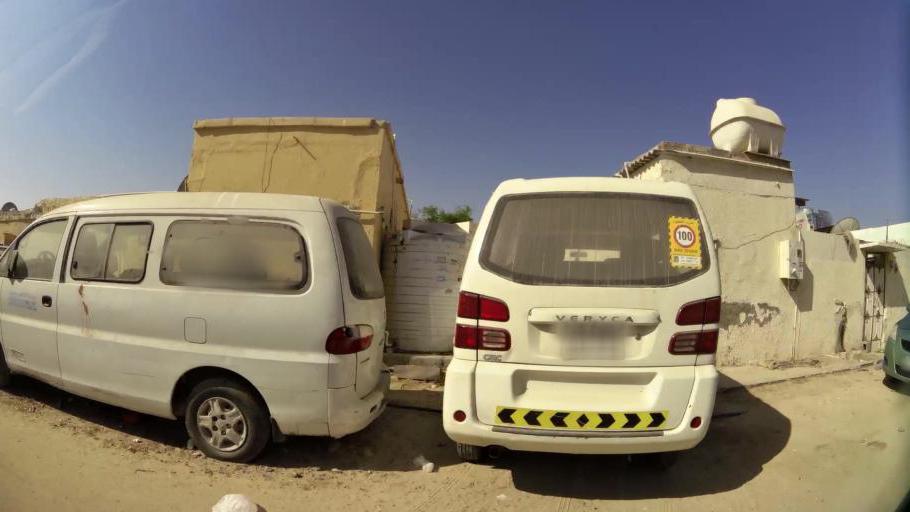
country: AE
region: Ajman
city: Ajman
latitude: 25.4144
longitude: 55.4487
